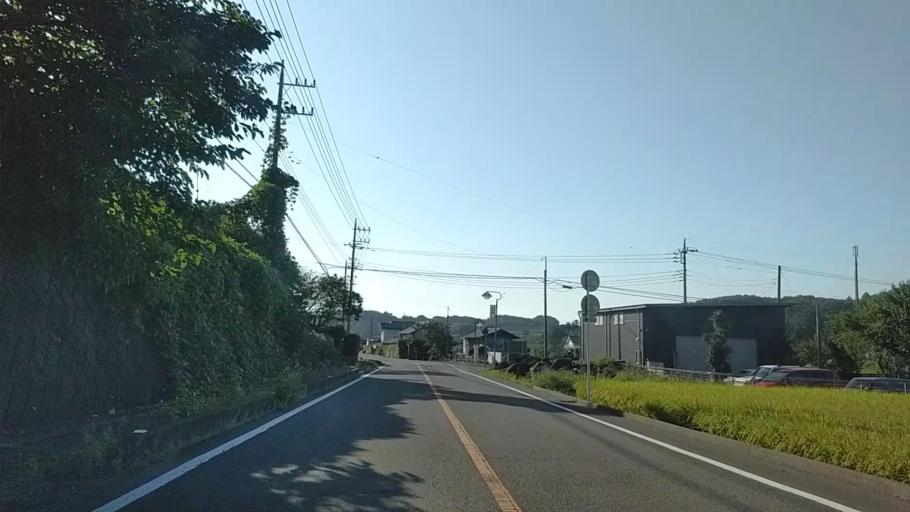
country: JP
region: Gunma
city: Annaka
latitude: 36.3503
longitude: 138.8690
